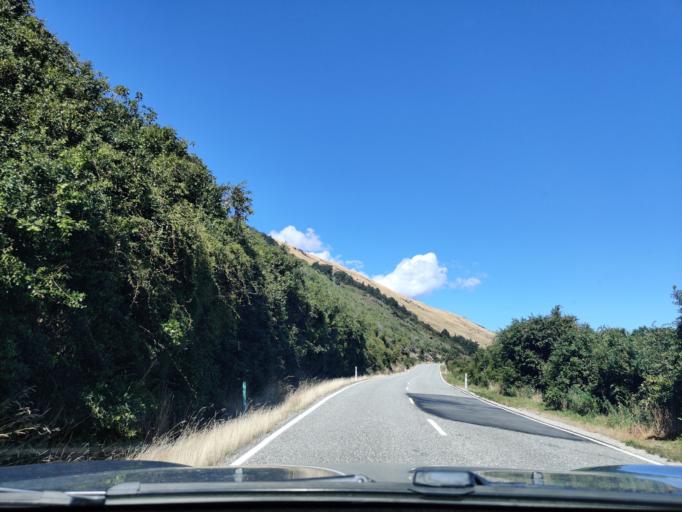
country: NZ
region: Otago
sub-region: Queenstown-Lakes District
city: Queenstown
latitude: -44.9509
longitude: 168.4362
